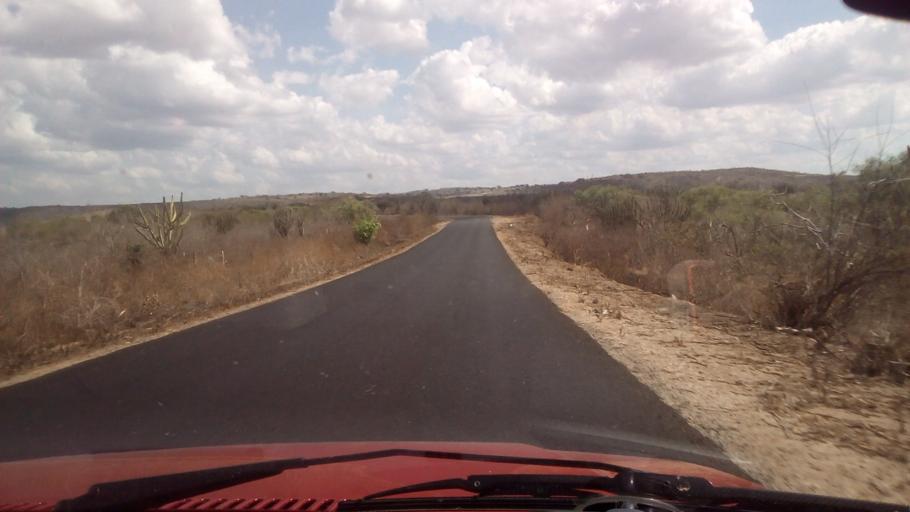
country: BR
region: Paraiba
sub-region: Bananeiras
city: Bananeiras
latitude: -6.7223
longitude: -35.7126
